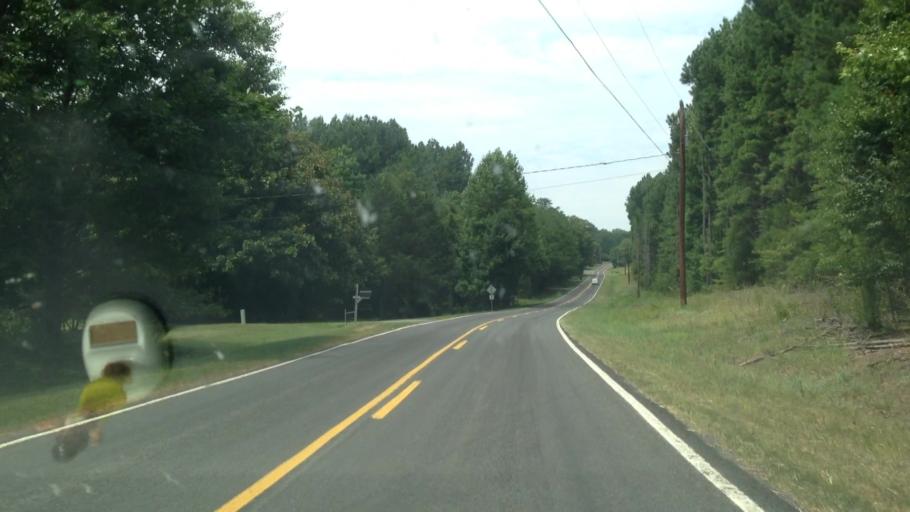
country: US
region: North Carolina
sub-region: Forsyth County
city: Walkertown
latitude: 36.1999
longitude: -80.1019
